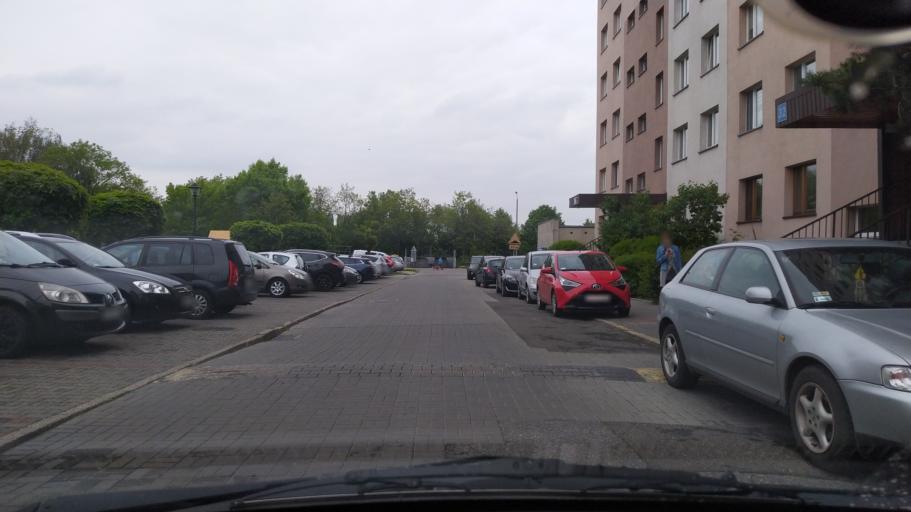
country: PL
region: Silesian Voivodeship
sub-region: Powiat gliwicki
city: Przyszowice
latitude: 50.2947
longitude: 18.7311
